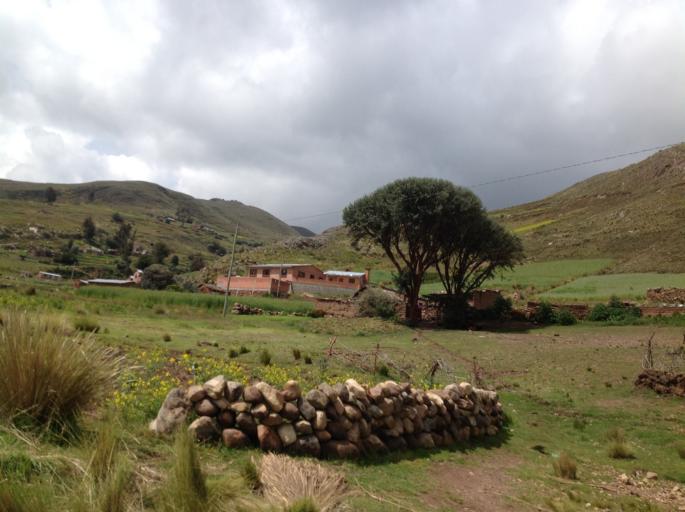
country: BO
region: La Paz
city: Yumani
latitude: -15.7731
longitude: -69.0032
